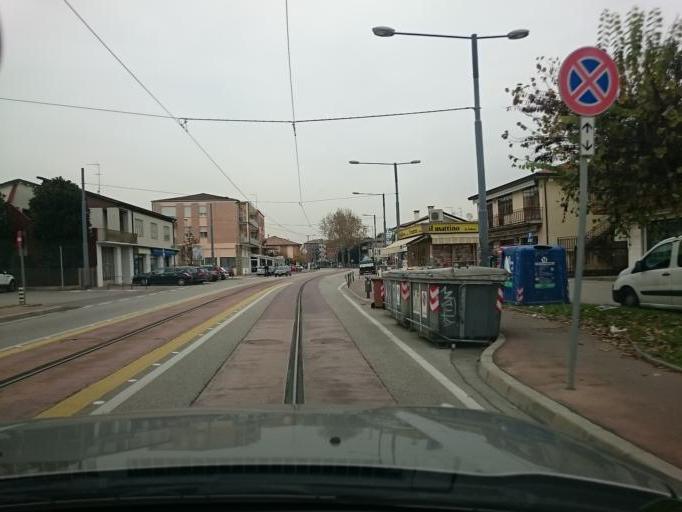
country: IT
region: Veneto
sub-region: Provincia di Padova
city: Mandriola-Sant'Agostino
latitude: 45.3747
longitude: 11.8706
